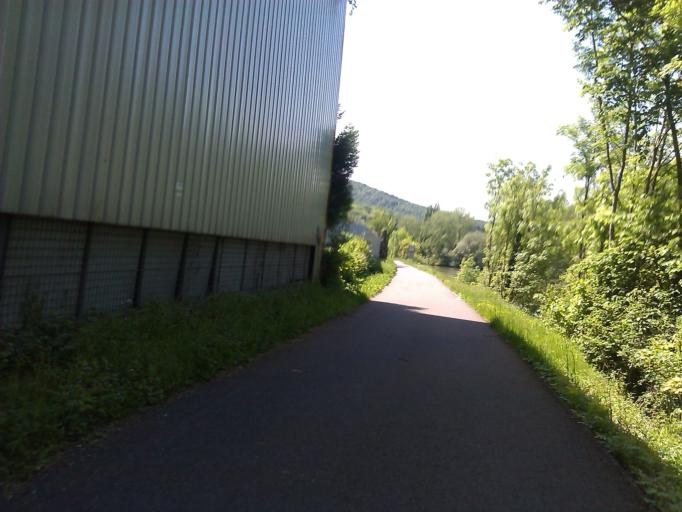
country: FR
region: Franche-Comte
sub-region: Departement du Doubs
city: Beure
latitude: 47.2164
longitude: 6.0073
